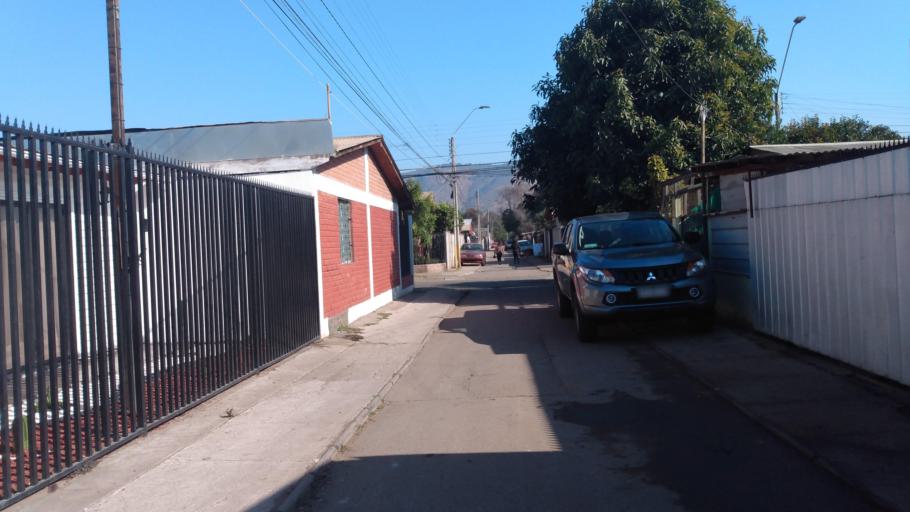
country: CL
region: Valparaiso
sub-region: Provincia de Quillota
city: Hacienda La Calera
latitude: -32.7302
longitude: -71.2061
